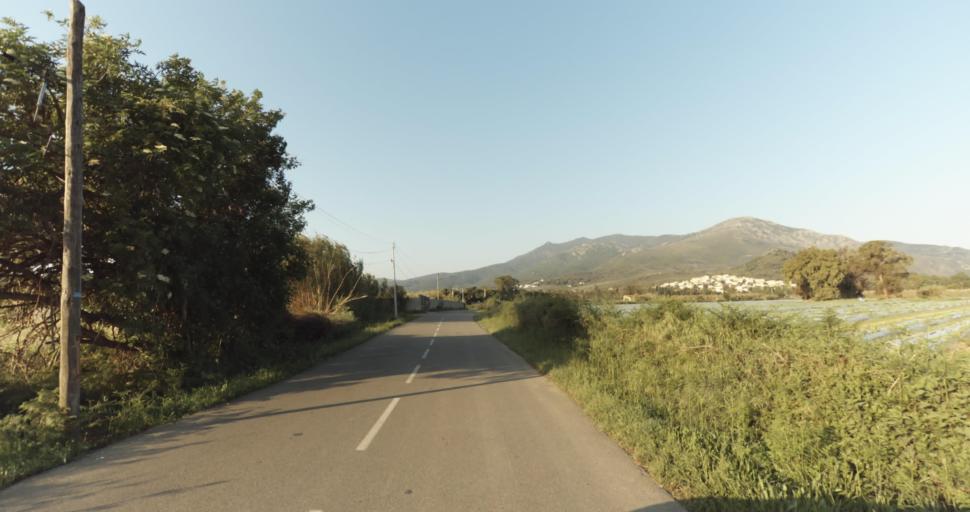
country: FR
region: Corsica
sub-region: Departement de la Haute-Corse
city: Biguglia
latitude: 42.6124
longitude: 9.4431
